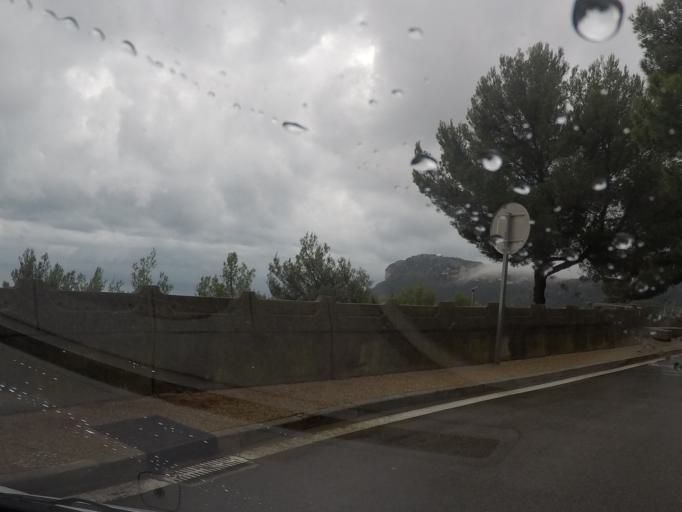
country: FR
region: Provence-Alpes-Cote d'Azur
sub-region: Departement des Alpes-Maritimes
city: Beausoleil
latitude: 43.7529
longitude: 7.4199
